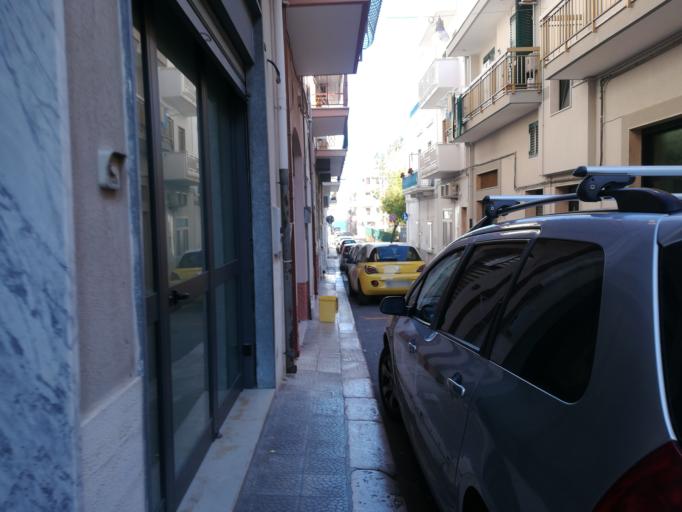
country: IT
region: Apulia
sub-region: Provincia di Bari
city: Polignano a Mare
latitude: 40.9939
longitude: 17.2243
